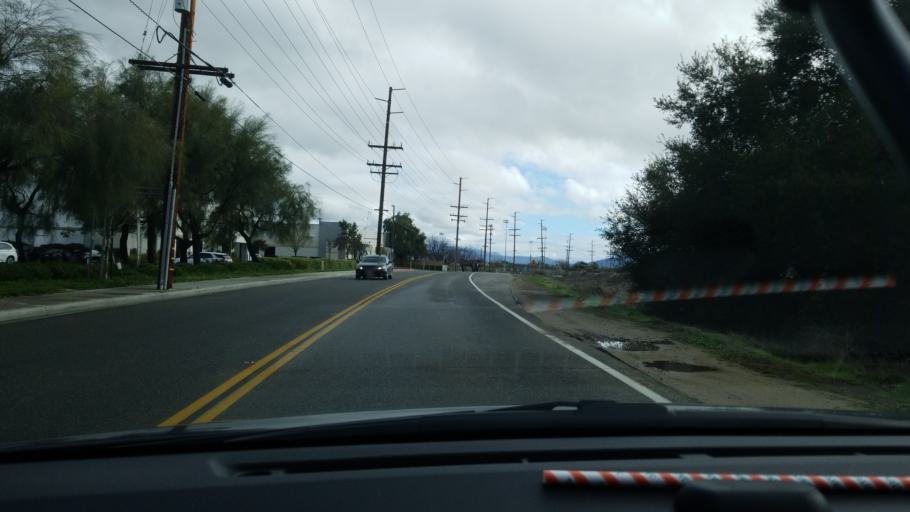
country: US
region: California
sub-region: Riverside County
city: Murrieta
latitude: 33.5398
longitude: -117.1916
